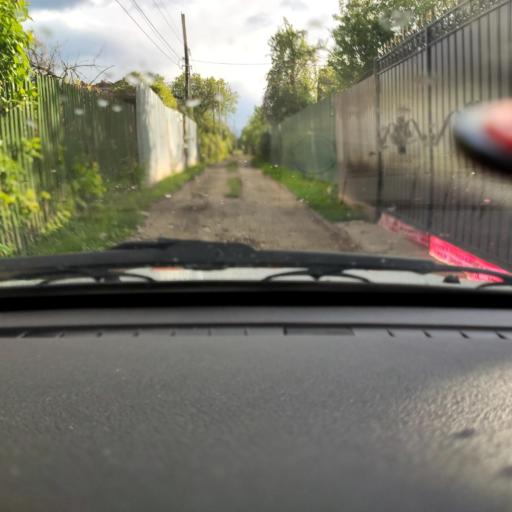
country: RU
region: Voronezj
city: Shilovo
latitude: 51.5870
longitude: 39.1597
